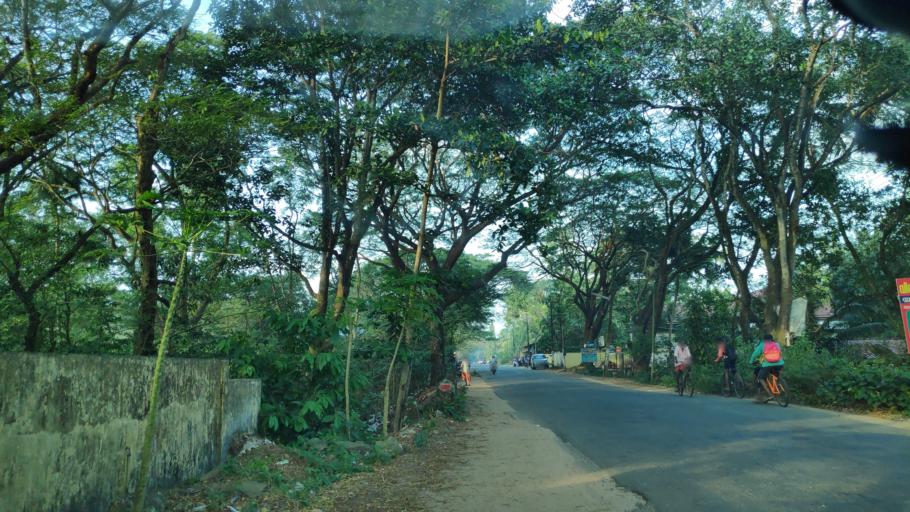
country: IN
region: Kerala
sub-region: Alappuzha
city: Shertallai
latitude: 9.6159
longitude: 76.3636
